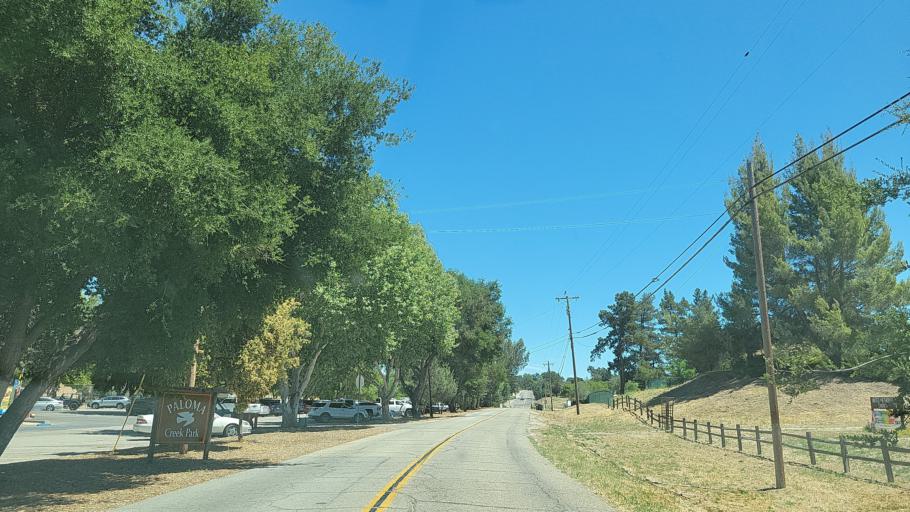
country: US
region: California
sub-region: San Luis Obispo County
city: Atascadero
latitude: 35.4533
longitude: -120.6354
